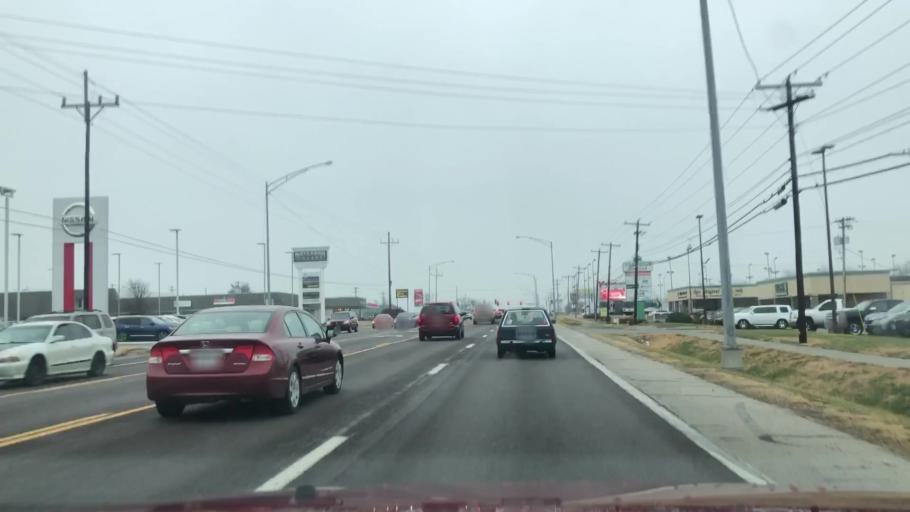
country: US
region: Missouri
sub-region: Greene County
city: Springfield
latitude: 37.1503
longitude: -93.2957
